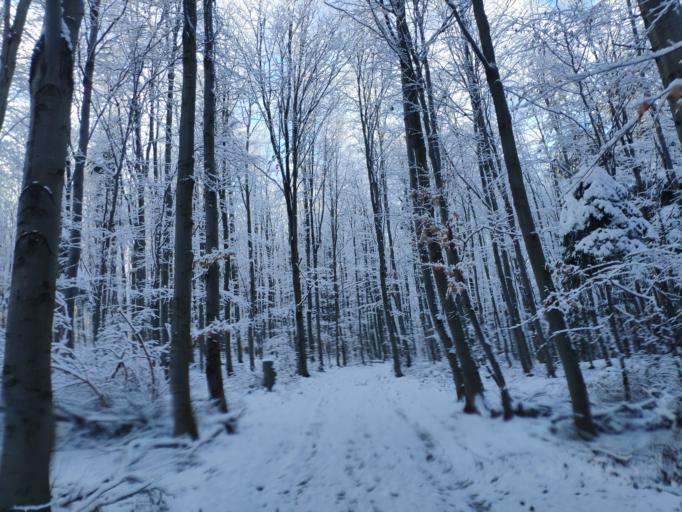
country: SK
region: Kosicky
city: Moldava nad Bodvou
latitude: 48.7460
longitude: 21.0858
